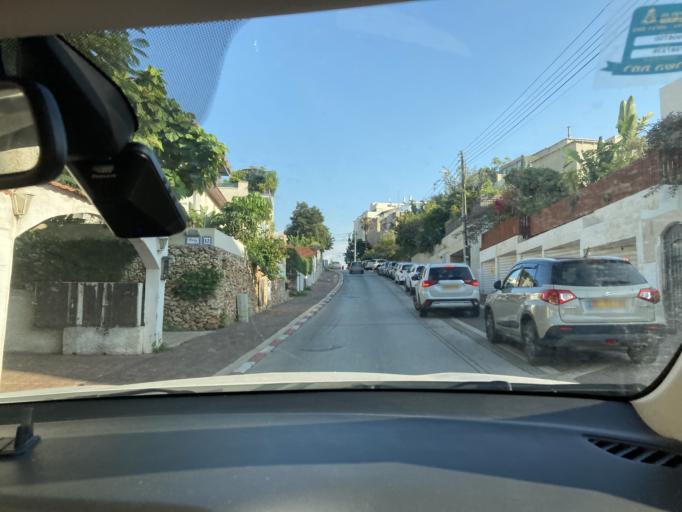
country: IL
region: Tel Aviv
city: Ramat HaSharon
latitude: 32.1497
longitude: 34.8383
